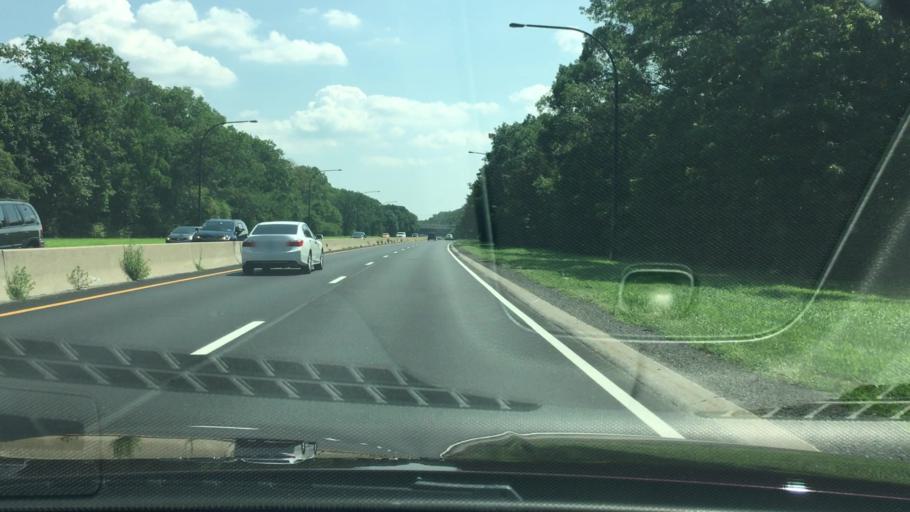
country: US
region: New York
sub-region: Nassau County
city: Salisbury
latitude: 40.7529
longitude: -73.5491
